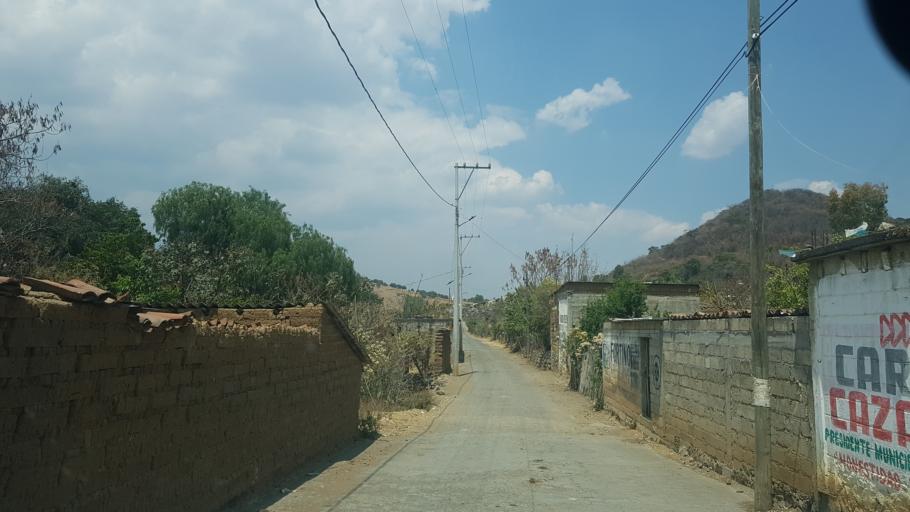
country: MX
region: Puebla
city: San Juan Amecac
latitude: 18.8054
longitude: -98.6243
